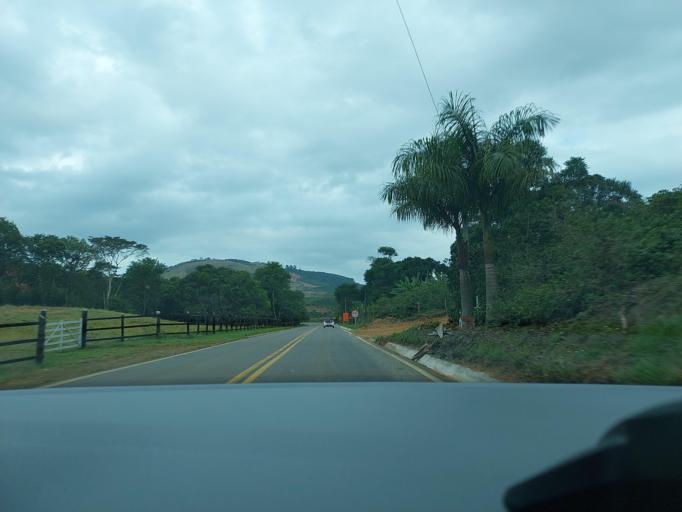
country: BR
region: Minas Gerais
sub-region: Mirai
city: Mirai
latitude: -20.9790
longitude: -42.5875
